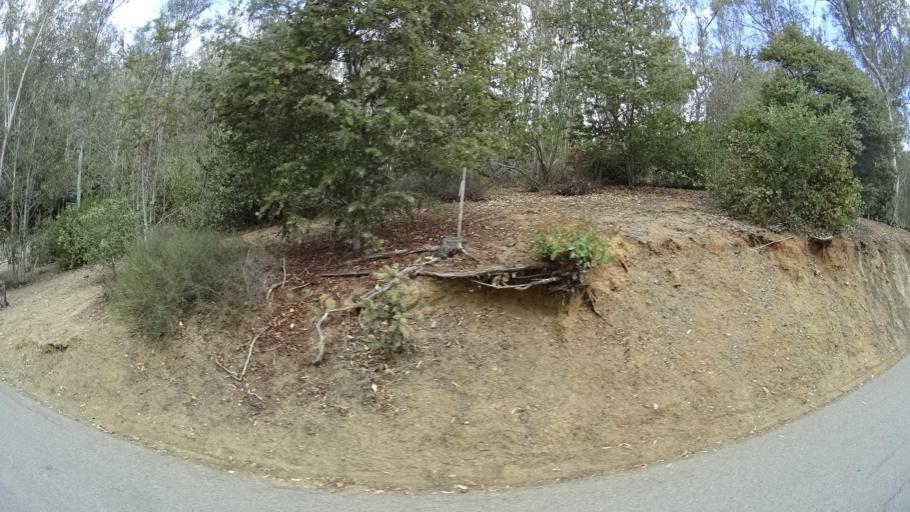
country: US
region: California
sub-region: San Diego County
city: Rancho Santa Fe
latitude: 33.0071
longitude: -117.2102
